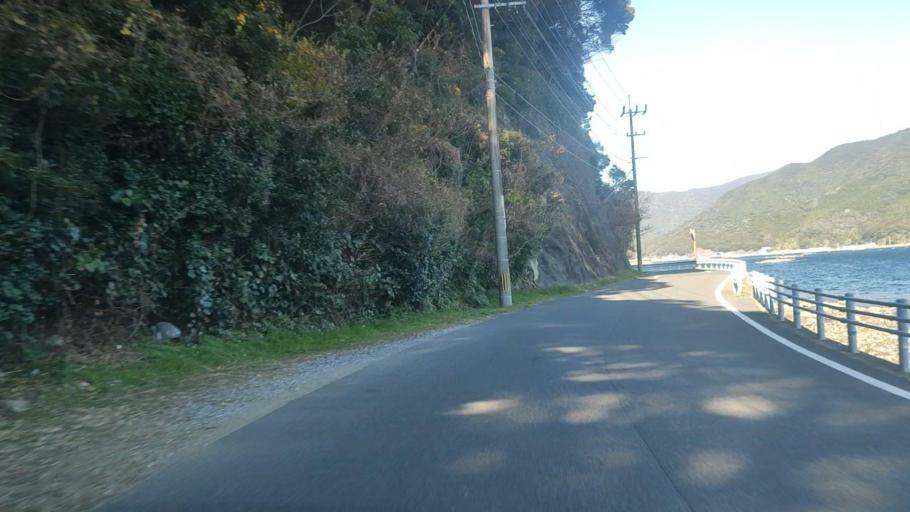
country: JP
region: Oita
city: Saiki
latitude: 32.8341
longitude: 131.9590
